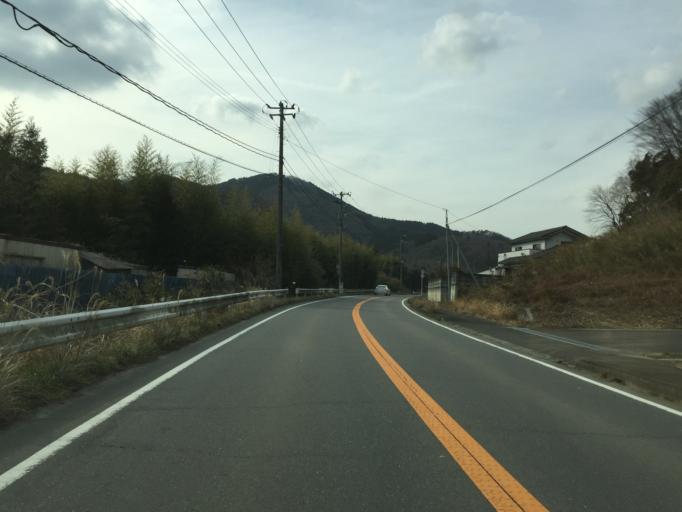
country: JP
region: Fukushima
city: Iwaki
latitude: 36.9644
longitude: 140.7510
